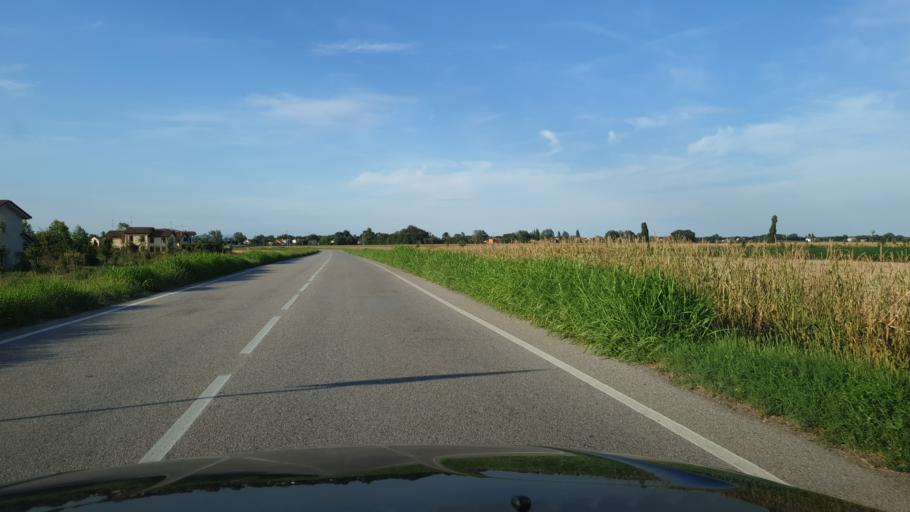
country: IT
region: Veneto
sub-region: Provincia di Rovigo
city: Pincara
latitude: 44.9924
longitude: 11.6149
